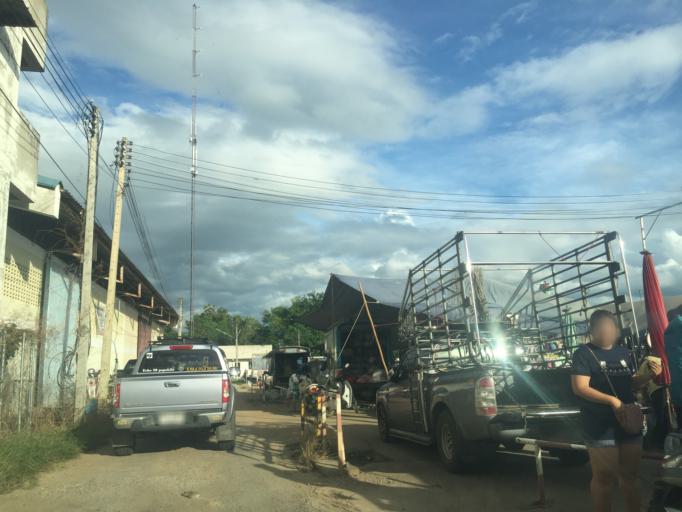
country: TH
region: Lamphun
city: Lamphun
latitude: 18.5589
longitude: 99.0370
